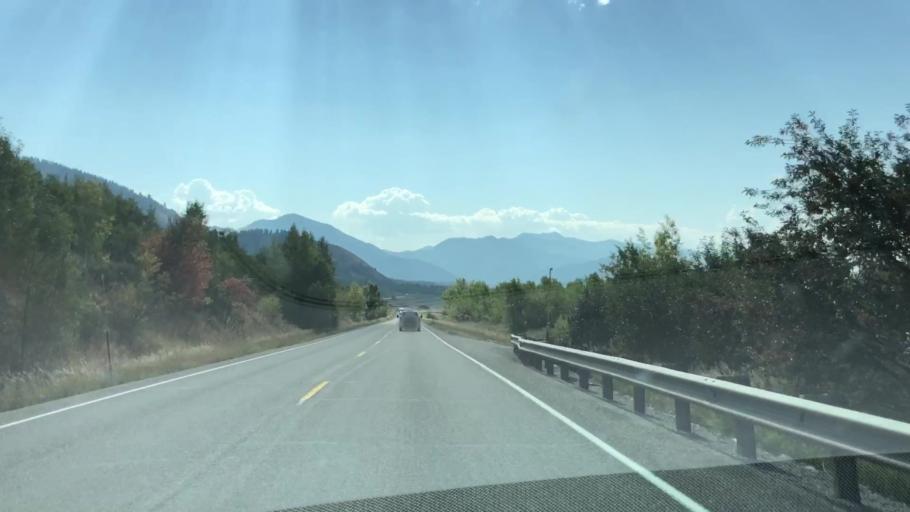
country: US
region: Wyoming
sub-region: Teton County
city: Hoback
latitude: 43.2238
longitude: -111.0772
